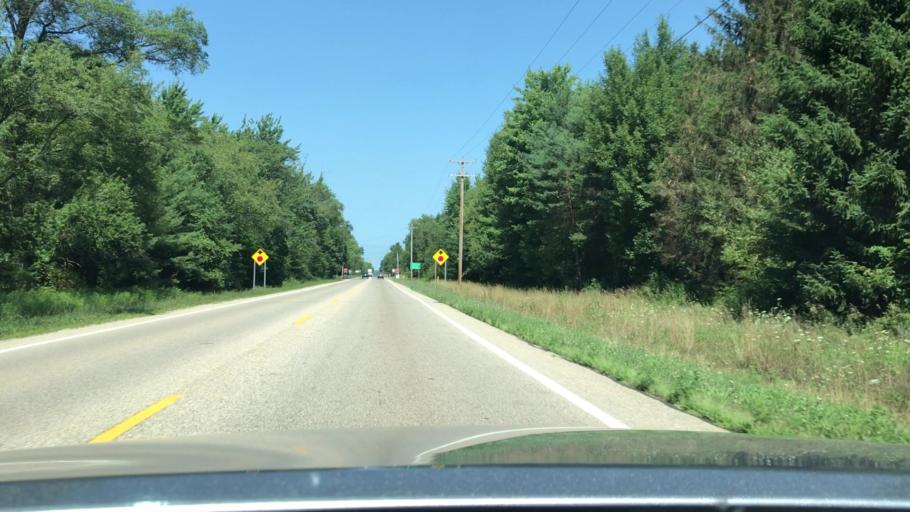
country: US
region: Michigan
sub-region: Ottawa County
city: Allendale
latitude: 42.9404
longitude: -86.0820
